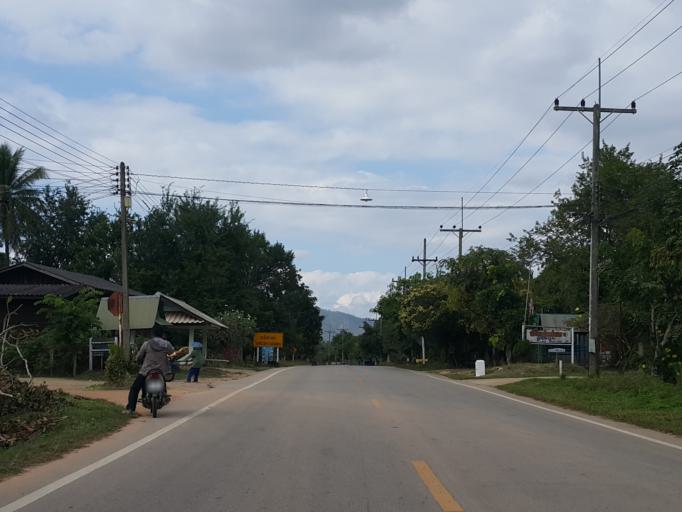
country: TH
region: Lampang
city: Chae Hom
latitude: 18.5689
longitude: 99.4722
